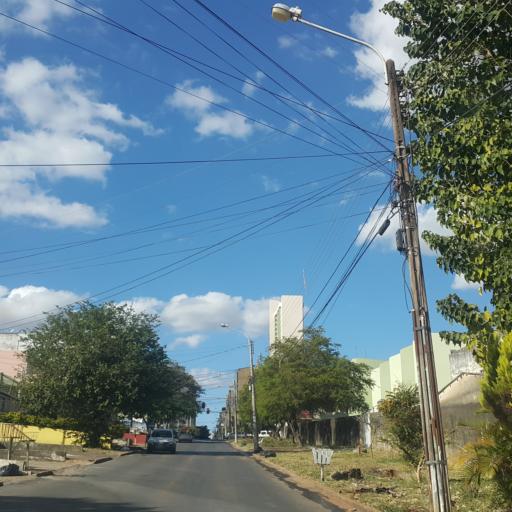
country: BR
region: Federal District
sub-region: Brasilia
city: Brasilia
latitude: -15.8279
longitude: -48.0640
